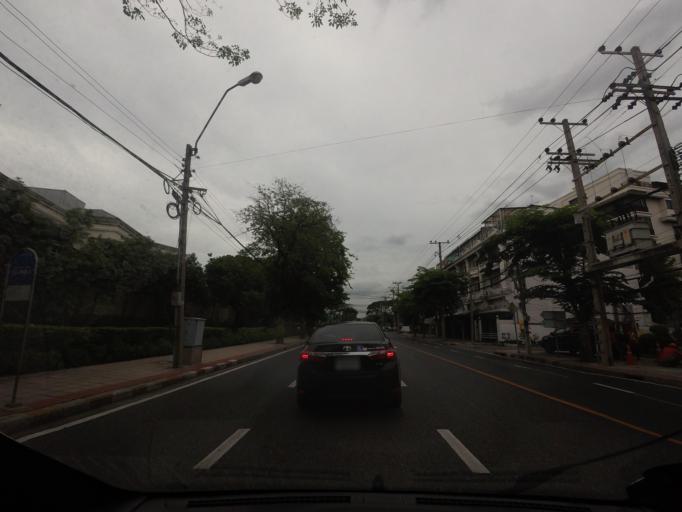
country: TH
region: Bangkok
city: Dusit
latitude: 13.7827
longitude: 100.5240
